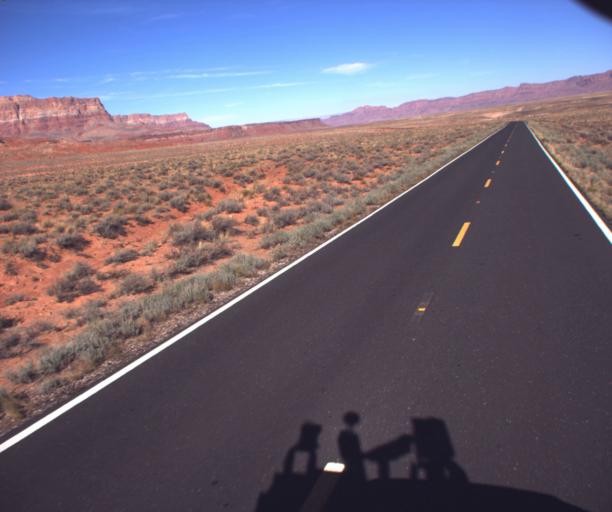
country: US
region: Arizona
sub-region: Coconino County
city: LeChee
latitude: 36.7029
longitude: -111.7914
